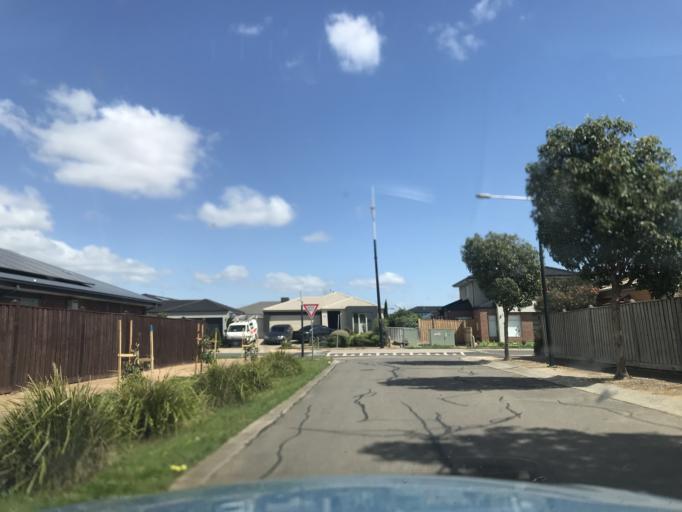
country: AU
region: Victoria
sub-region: Wyndham
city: Williams Landing
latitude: -37.8551
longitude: 144.7336
